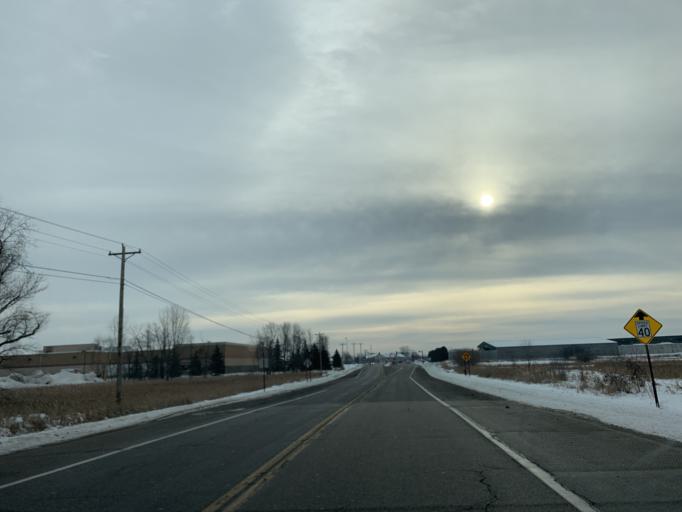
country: US
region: Minnesota
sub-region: Washington County
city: Forest Lake
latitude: 45.2839
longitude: -93.0134
